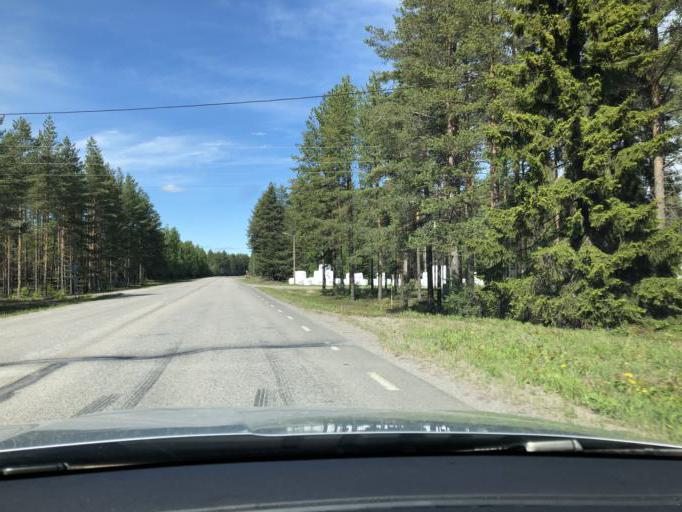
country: SE
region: Norrbotten
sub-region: Pitea Kommun
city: Bergsviken
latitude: 65.3647
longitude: 21.3657
